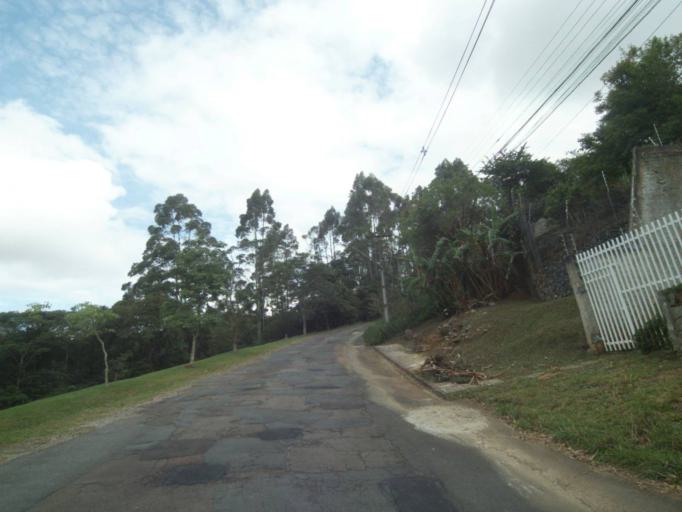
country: BR
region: Parana
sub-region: Curitiba
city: Curitiba
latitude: -25.3801
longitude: -49.2866
